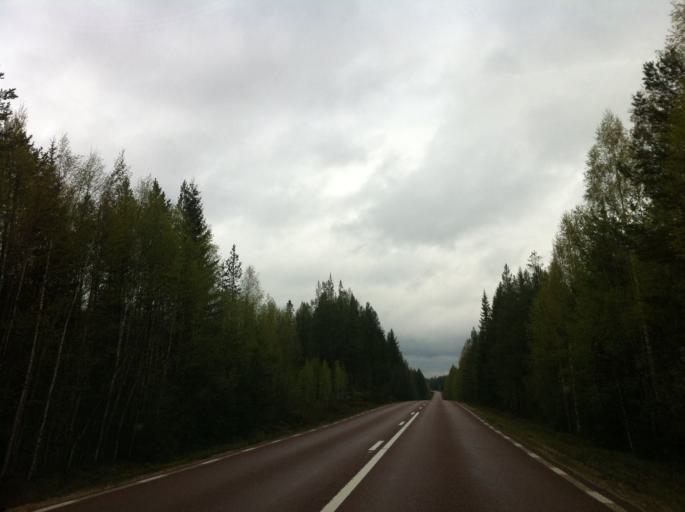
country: SE
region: Jaemtland
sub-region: Harjedalens Kommun
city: Sveg
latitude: 61.8782
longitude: 14.6285
